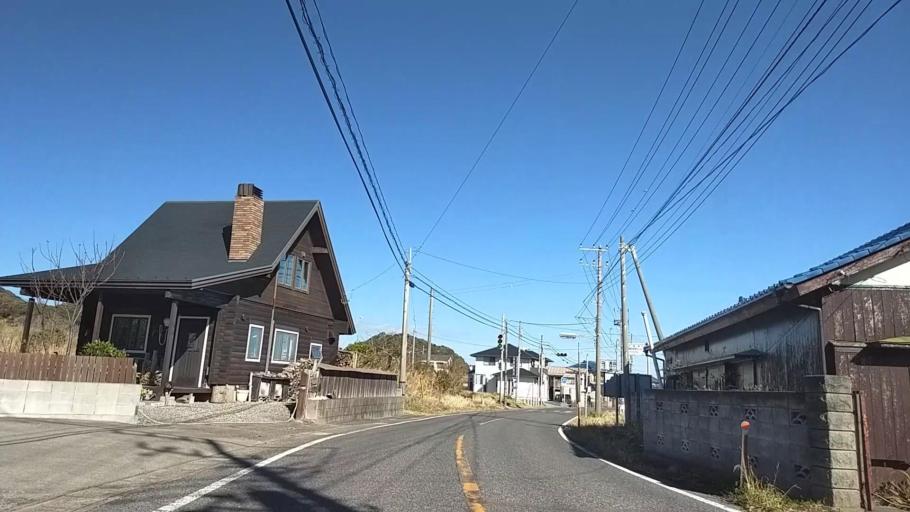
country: JP
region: Chiba
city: Tateyama
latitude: 34.9407
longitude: 139.9566
